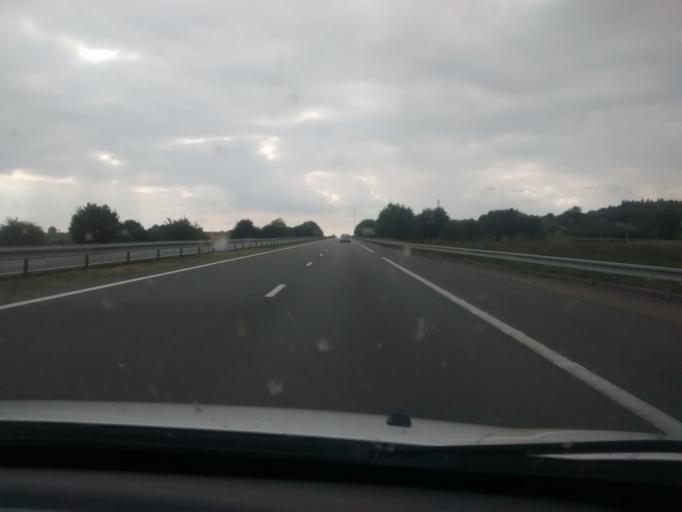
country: FR
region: Pays de la Loire
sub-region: Departement de la Sarthe
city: Brulon
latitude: 48.0080
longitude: -0.2224
